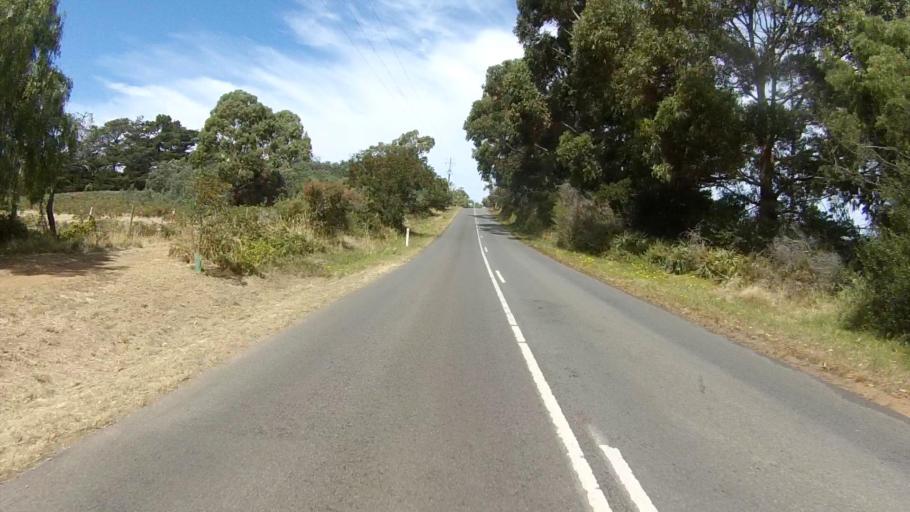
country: AU
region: Tasmania
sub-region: Kingborough
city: Taroona
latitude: -43.0138
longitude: 147.4146
